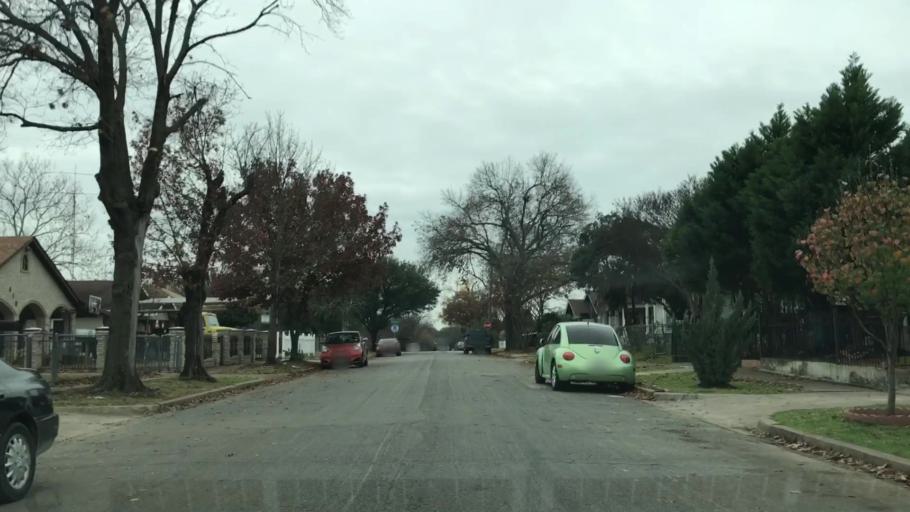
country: US
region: Texas
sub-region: Dallas County
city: Cockrell Hill
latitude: 32.7403
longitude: -96.8491
